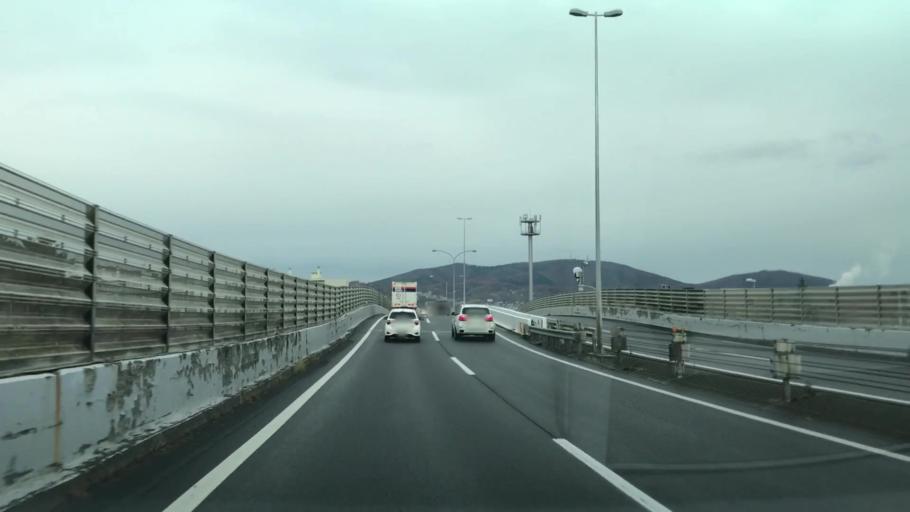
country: JP
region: Hokkaido
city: Otaru
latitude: 43.1808
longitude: 141.0205
